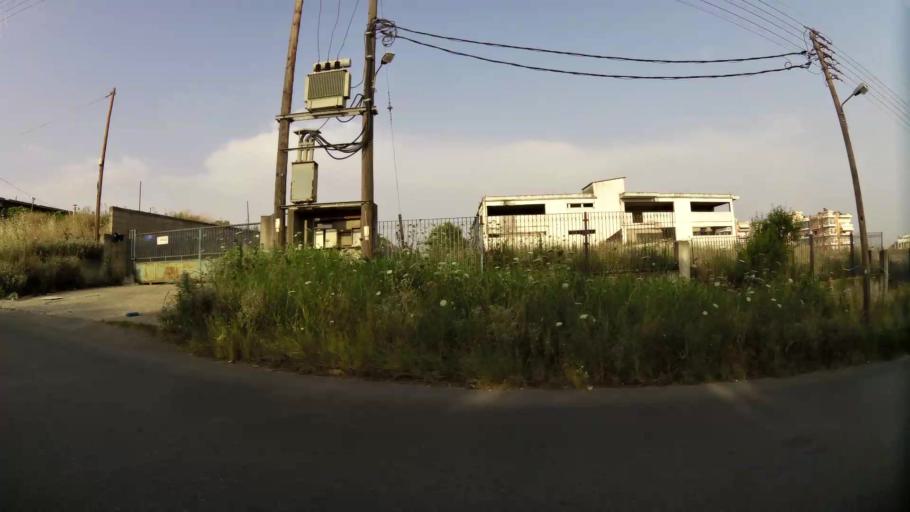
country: GR
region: Central Macedonia
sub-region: Nomos Thessalonikis
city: Evosmos
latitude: 40.6847
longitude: 22.9061
